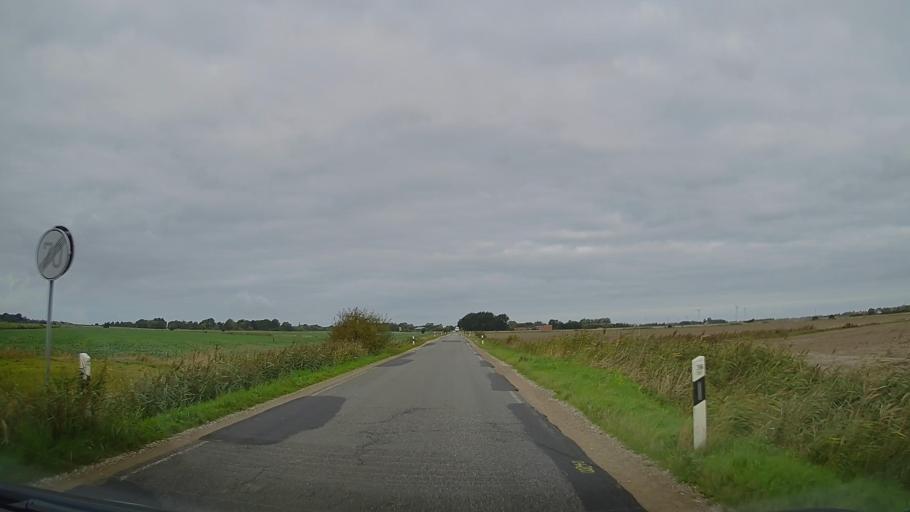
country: DE
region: Schleswig-Holstein
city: Emmelsbull-Horsbull
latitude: 54.8022
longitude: 8.7138
